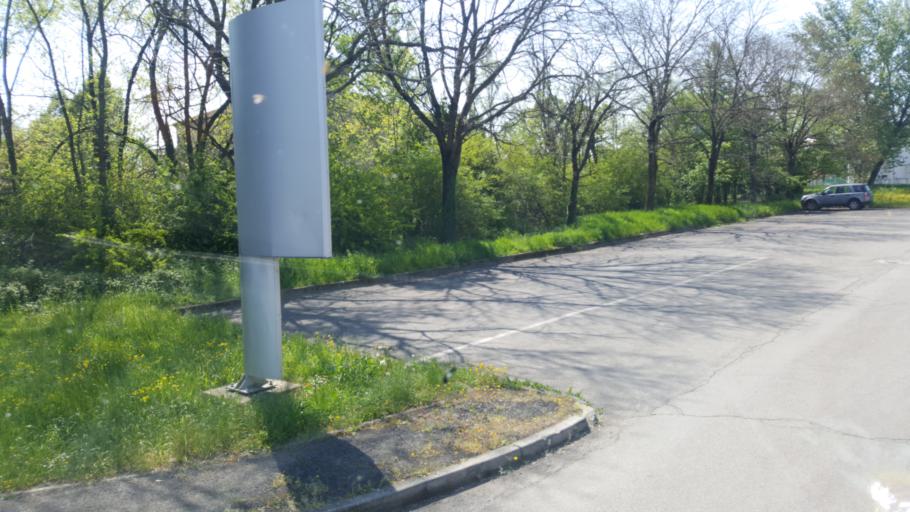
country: IT
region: Emilia-Romagna
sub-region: Provincia di Reggio Emilia
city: Bagnolo in Piano
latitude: 44.7352
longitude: 10.6560
